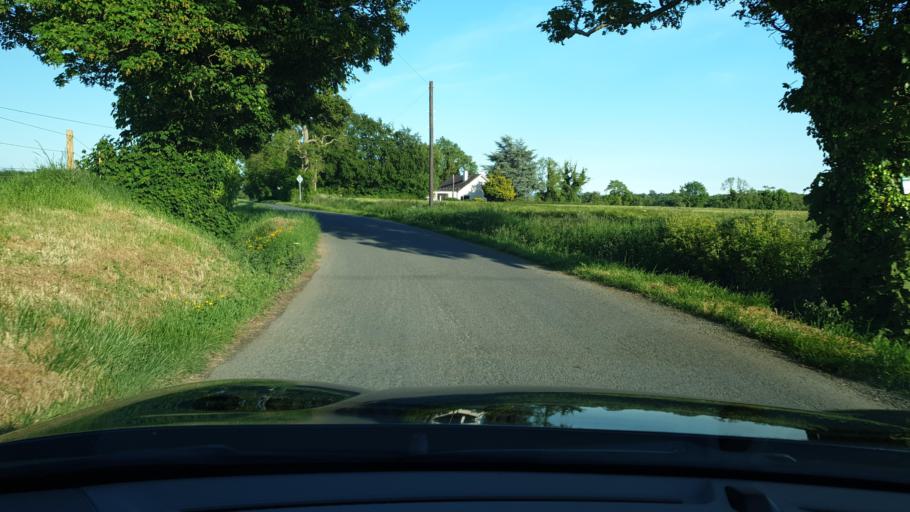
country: IE
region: Leinster
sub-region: Fingal County
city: Swords
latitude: 53.5032
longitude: -6.2402
